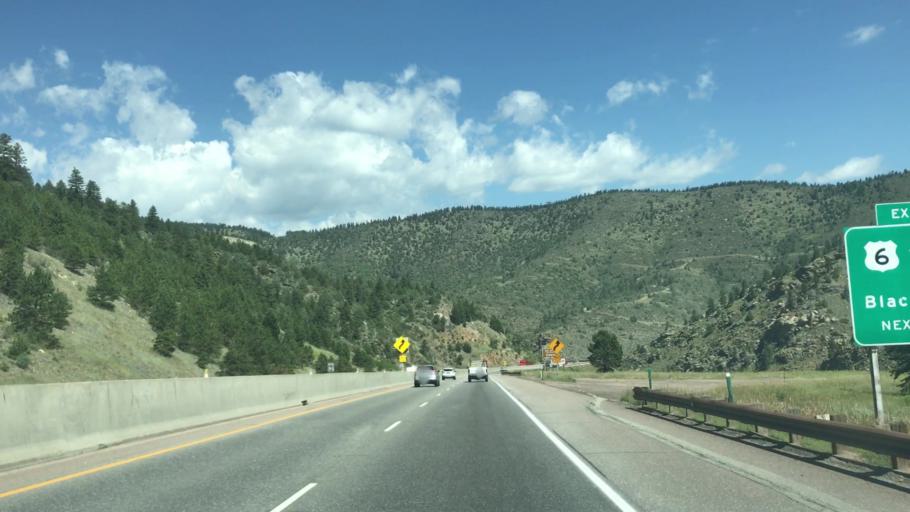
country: US
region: Colorado
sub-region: Clear Creek County
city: Idaho Springs
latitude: 39.7386
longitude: -105.4316
